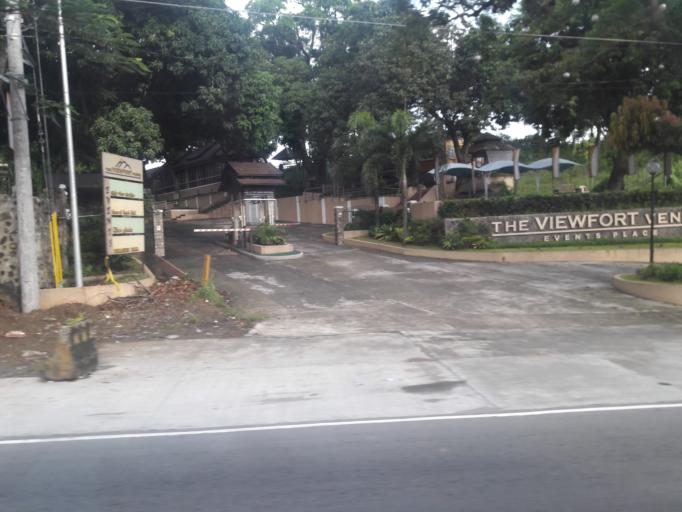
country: PH
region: Calabarzon
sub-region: Province of Cavite
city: Carmona
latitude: 14.3102
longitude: 121.0336
